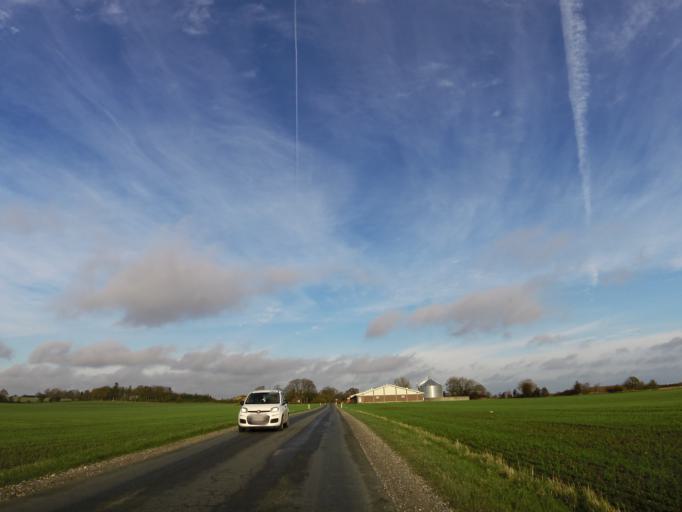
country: DK
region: Central Jutland
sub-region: Odder Kommune
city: Odder
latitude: 55.9336
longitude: 10.2359
